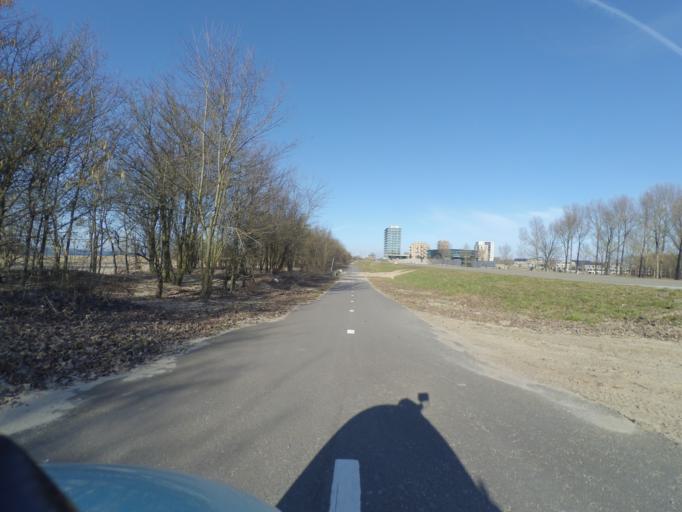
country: NL
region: North Holland
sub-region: Gemeente Naarden
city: Naarden
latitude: 52.3356
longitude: 5.1420
